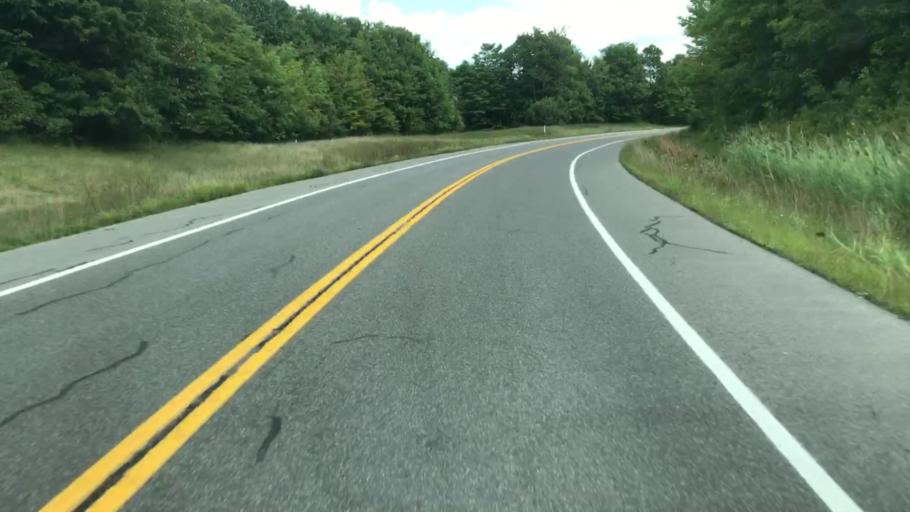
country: US
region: New York
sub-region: Onondaga County
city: Marcellus
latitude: 42.9535
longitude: -76.3698
